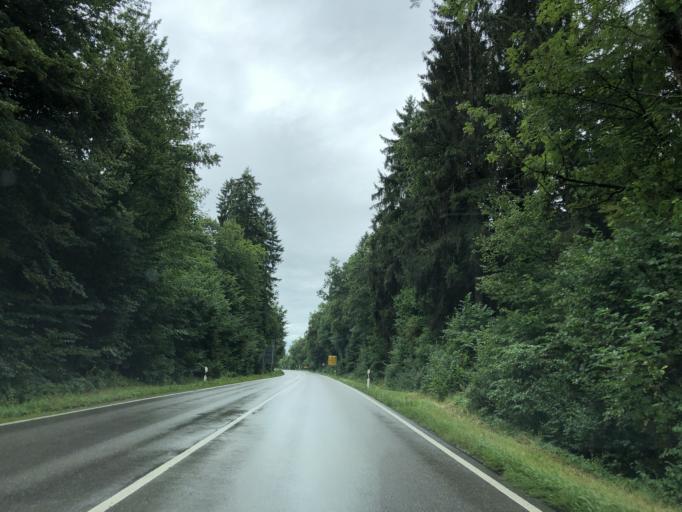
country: DE
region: Bavaria
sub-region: Upper Bavaria
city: Sauerlach
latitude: 48.0009
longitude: 11.6403
